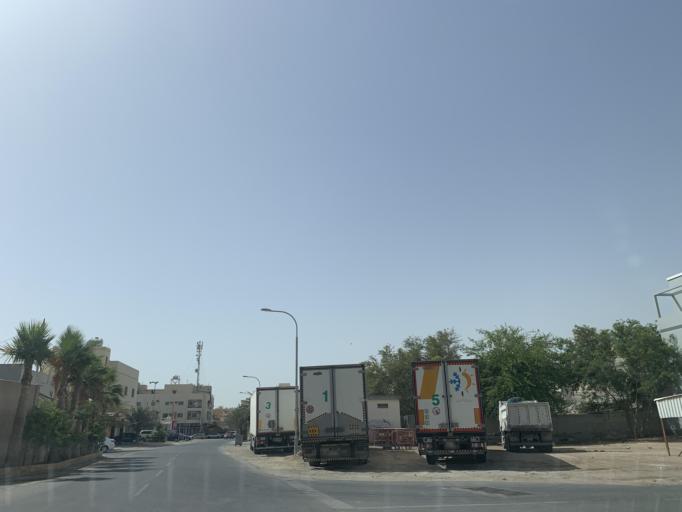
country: BH
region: Northern
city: Ar Rifa'
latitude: 26.1508
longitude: 50.5802
